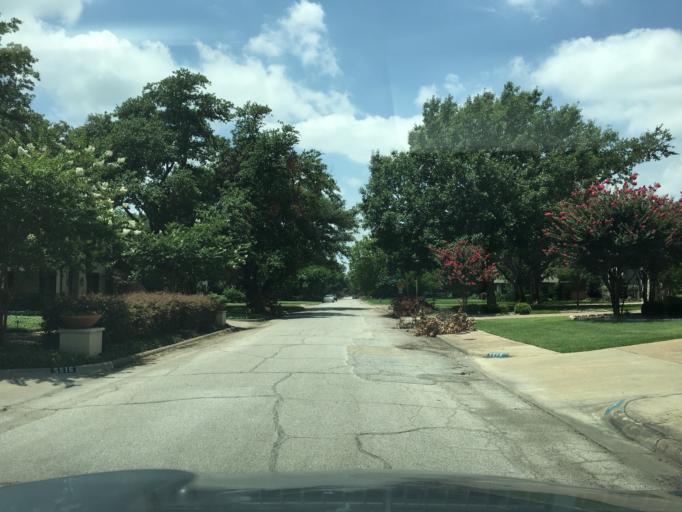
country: US
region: Texas
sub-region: Dallas County
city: Addison
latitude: 32.9176
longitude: -96.8064
